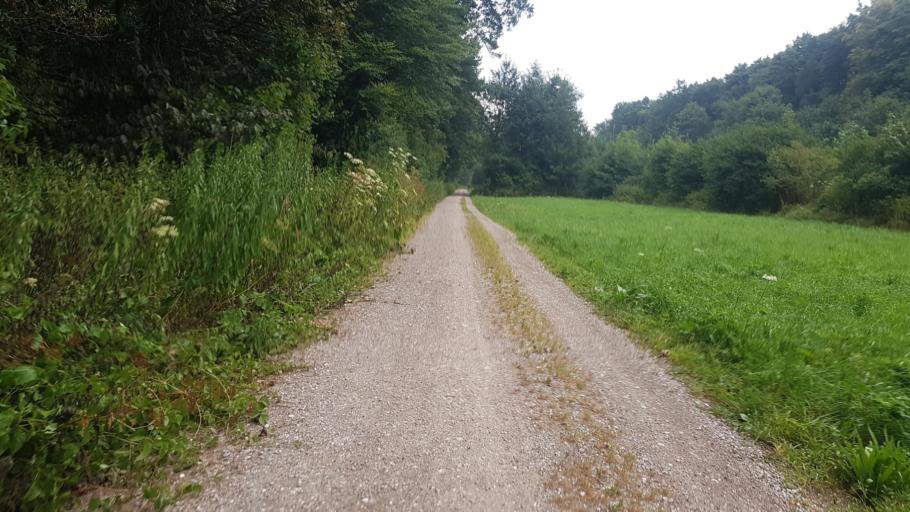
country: DE
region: Bavaria
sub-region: Upper Bavaria
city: Gauting
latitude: 48.0482
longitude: 11.3607
